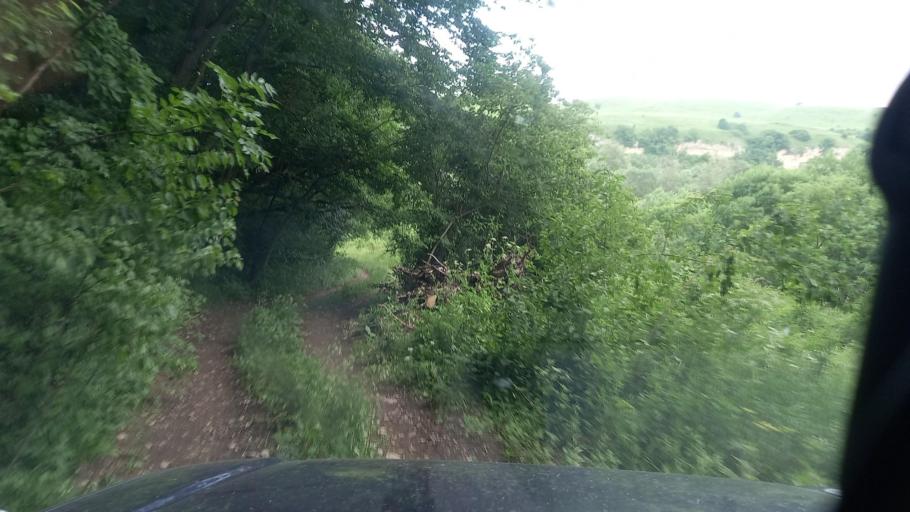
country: RU
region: Krasnodarskiy
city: Peredovaya
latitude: 44.0802
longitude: 41.3506
